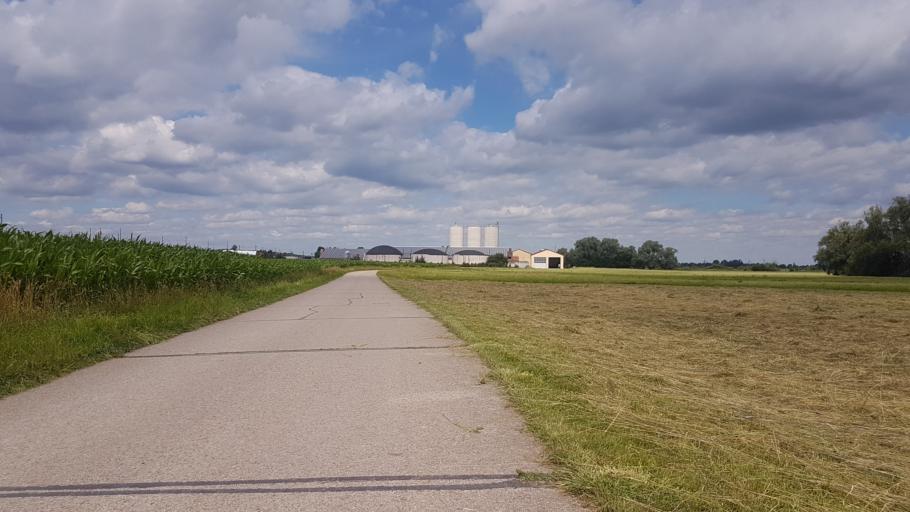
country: DE
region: Bavaria
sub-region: Regierungsbezirk Mittelfranken
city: Gunzenhausen
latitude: 49.0892
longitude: 10.7638
